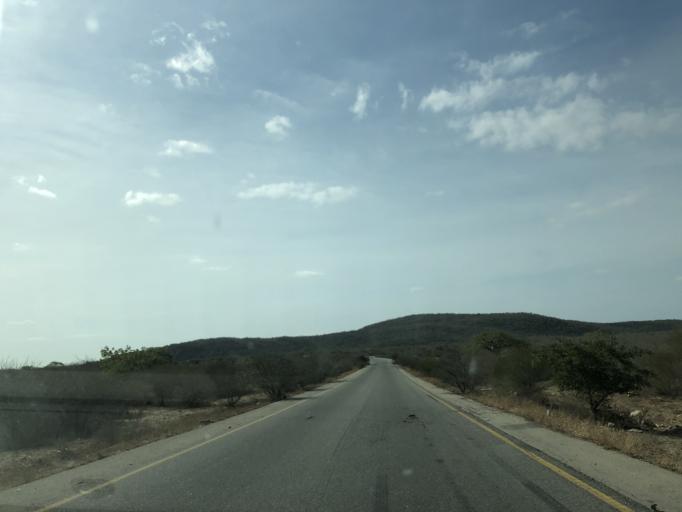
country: AO
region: Benguela
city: Benguela
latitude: -12.8960
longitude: 13.4953
